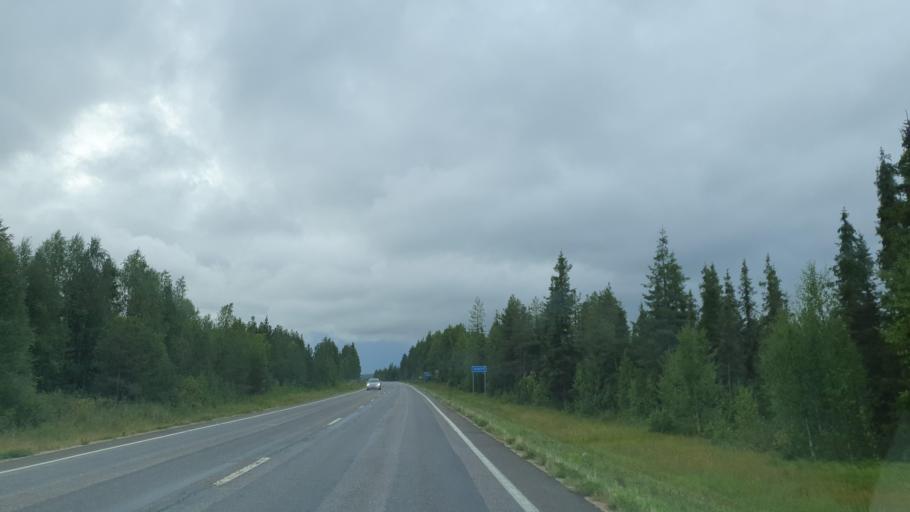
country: FI
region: Lapland
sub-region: Tunturi-Lappi
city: Kolari
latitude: 67.2136
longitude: 23.9044
